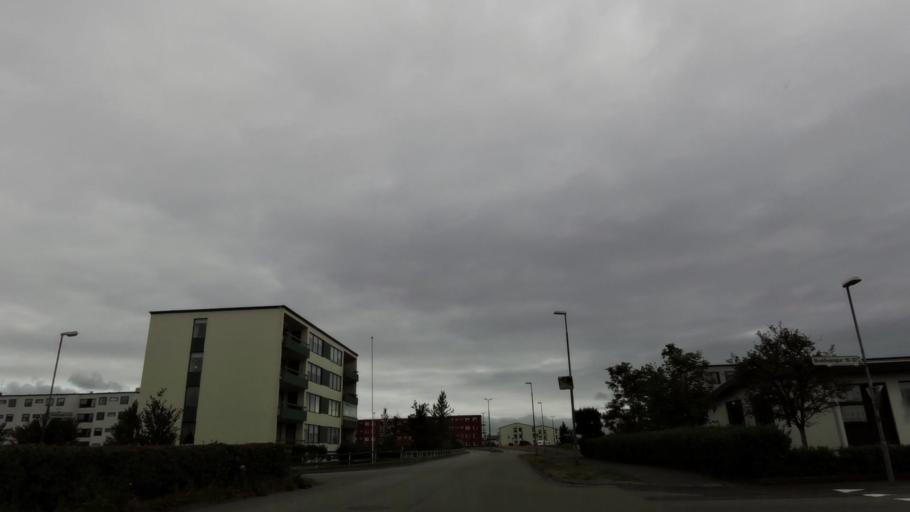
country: IS
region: Capital Region
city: Hafnarfjoerdur
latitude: 64.0810
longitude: -21.9613
